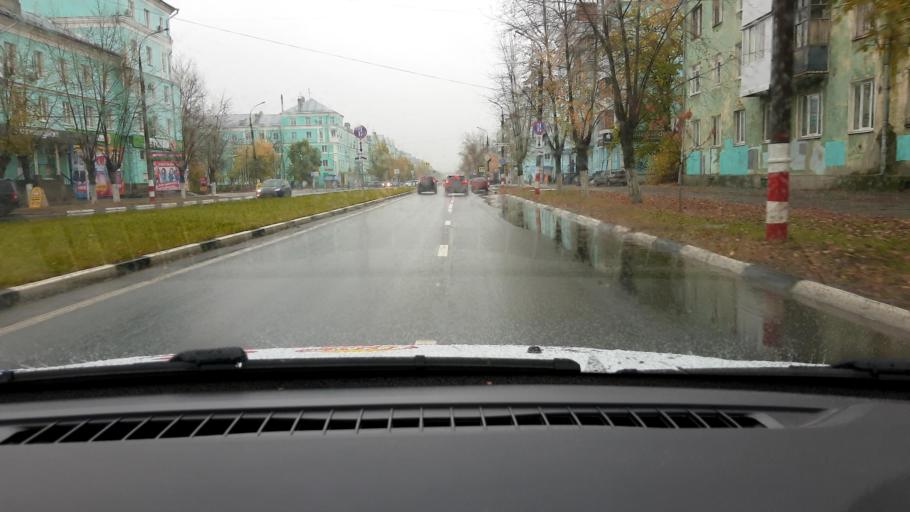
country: RU
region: Nizjnij Novgorod
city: Dzerzhinsk
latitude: 56.2423
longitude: 43.4437
